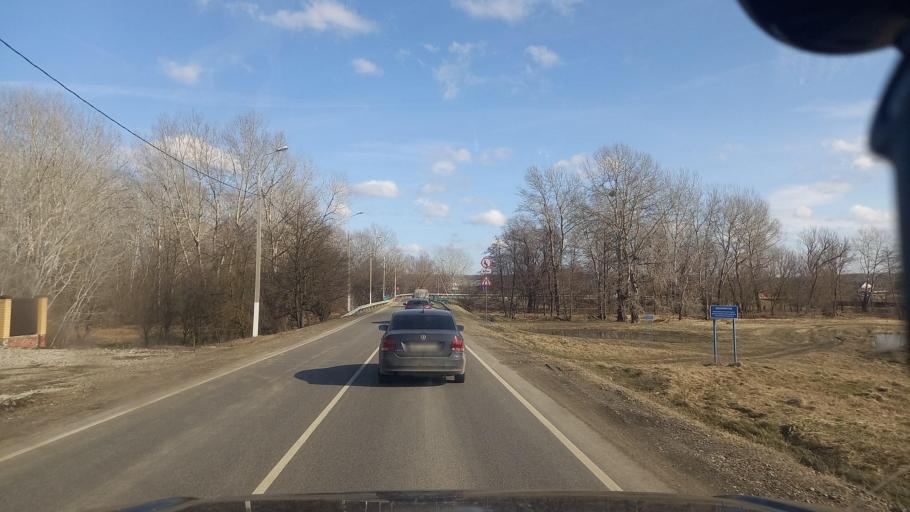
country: RU
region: Krasnodarskiy
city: Novodmitriyevskaya
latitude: 44.7771
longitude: 38.9738
